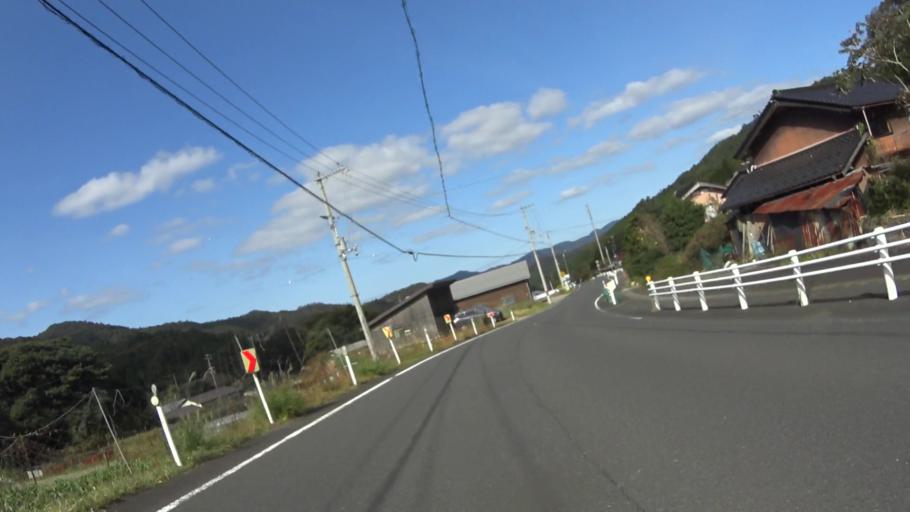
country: JP
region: Hyogo
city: Toyooka
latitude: 35.5433
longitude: 134.9779
